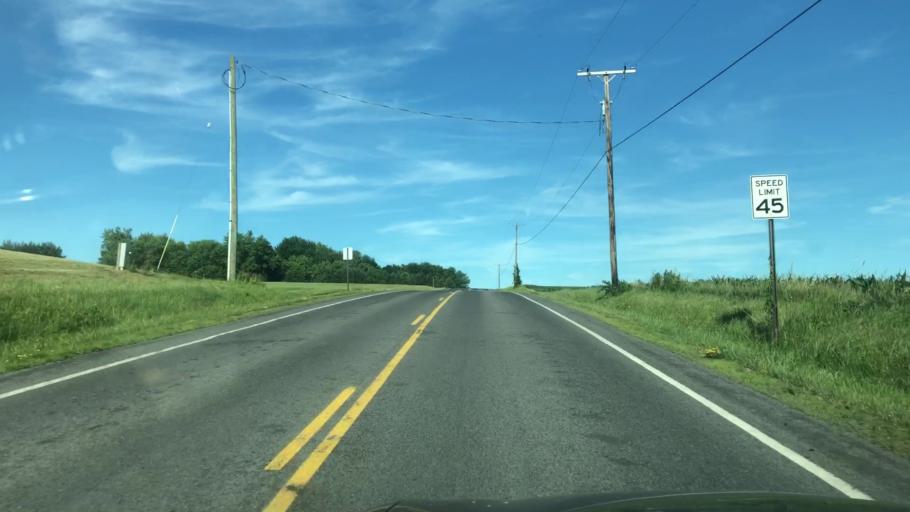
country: US
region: New York
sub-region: Wayne County
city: Macedon
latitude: 43.1163
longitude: -77.3087
